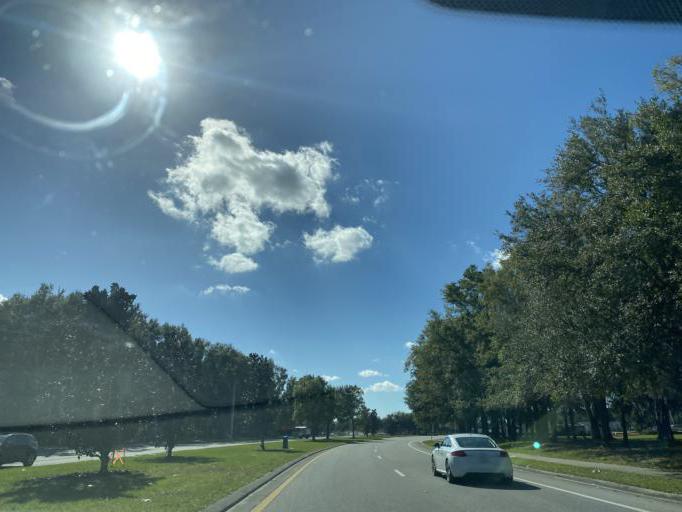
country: US
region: Florida
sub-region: Seminole County
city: Heathrow
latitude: 28.7953
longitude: -81.3546
